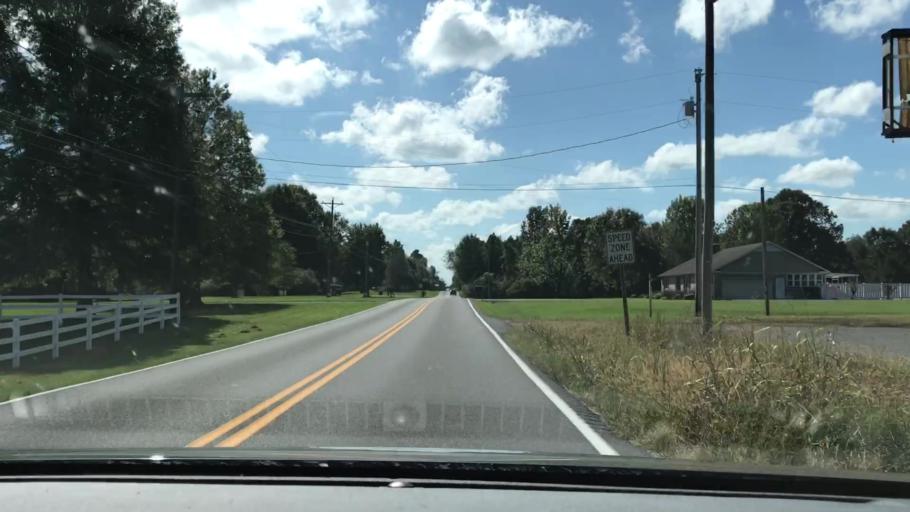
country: US
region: Kentucky
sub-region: McCracken County
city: Reidland
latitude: 36.9277
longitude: -88.5189
